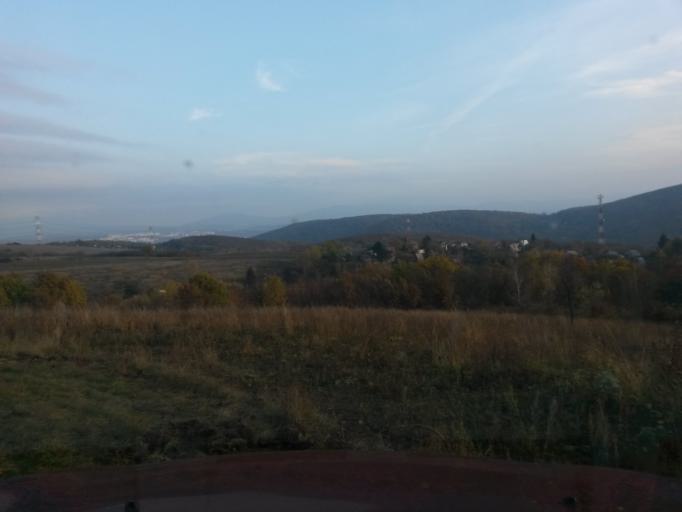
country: SK
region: Kosicky
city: Kosice
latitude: 48.7628
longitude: 21.1963
